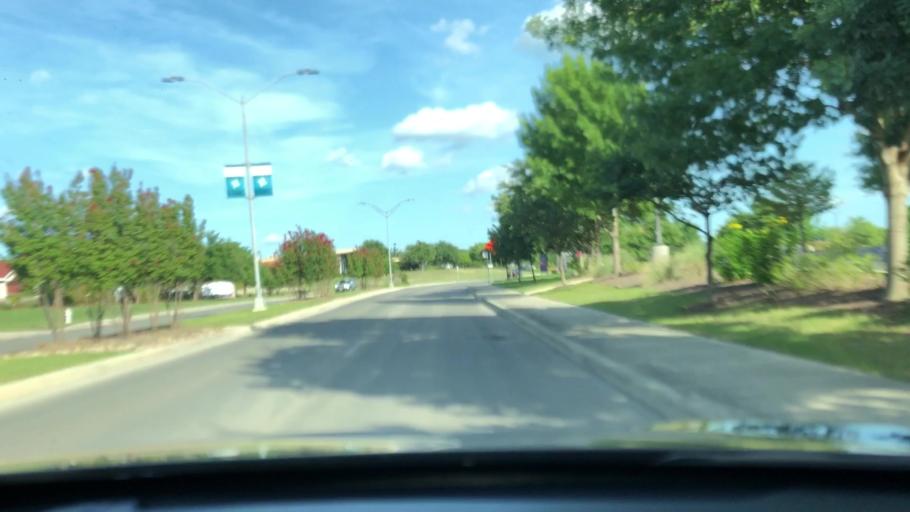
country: US
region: Texas
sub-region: Bexar County
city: Leon Valley
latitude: 29.5280
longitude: -98.5920
